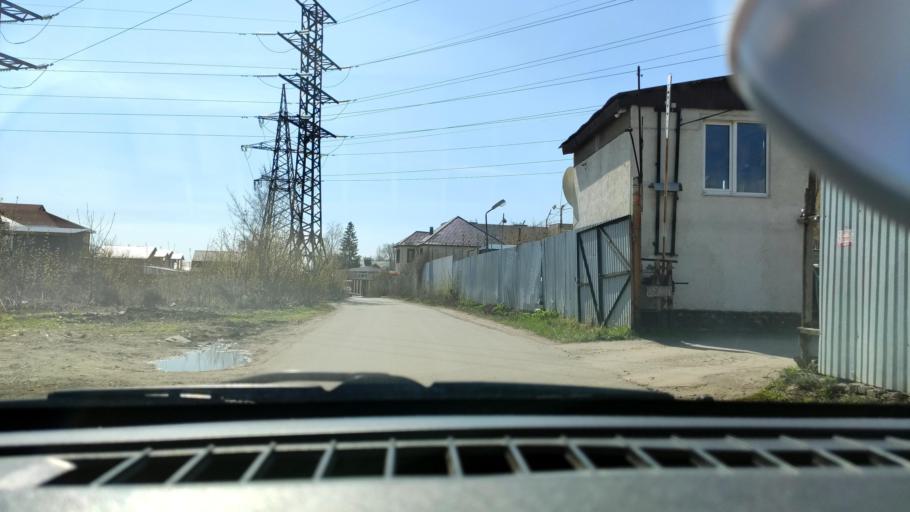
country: RU
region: Samara
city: Petra-Dubrava
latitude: 53.2943
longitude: 50.2918
